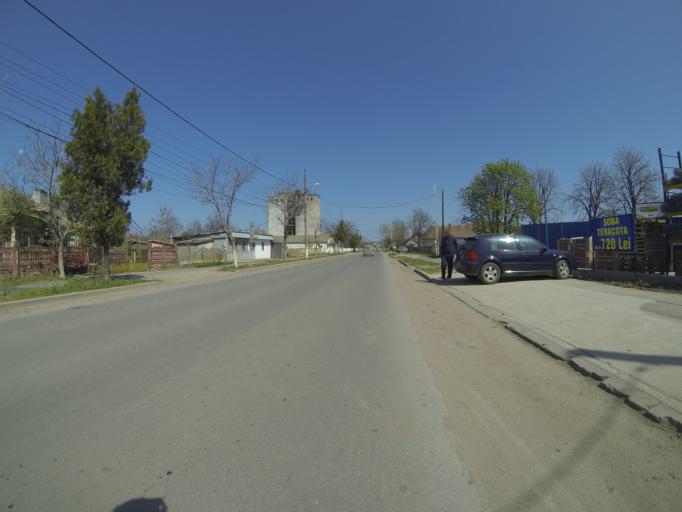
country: RO
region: Dolj
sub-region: Comuna Segarcea
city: Segarcea
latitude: 44.0896
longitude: 23.7312
